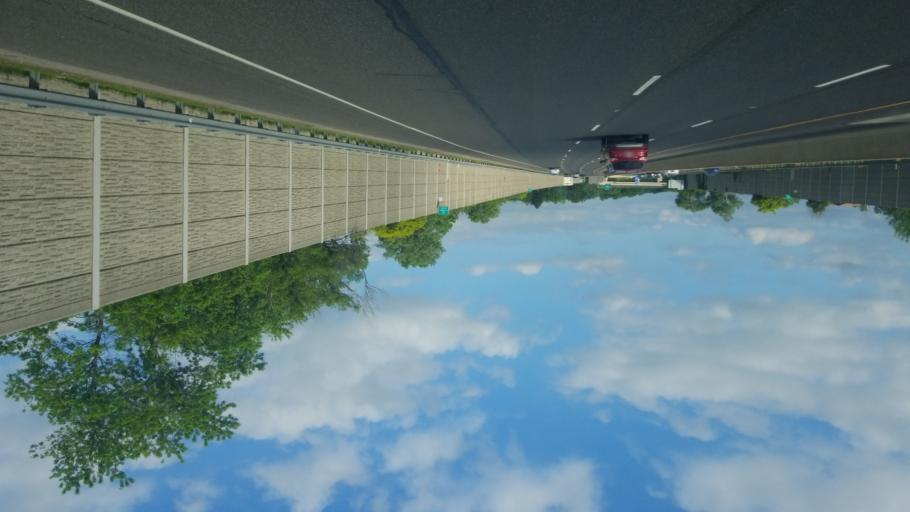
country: US
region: Indiana
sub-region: Allen County
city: Fort Wayne
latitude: 41.1439
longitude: -85.1227
